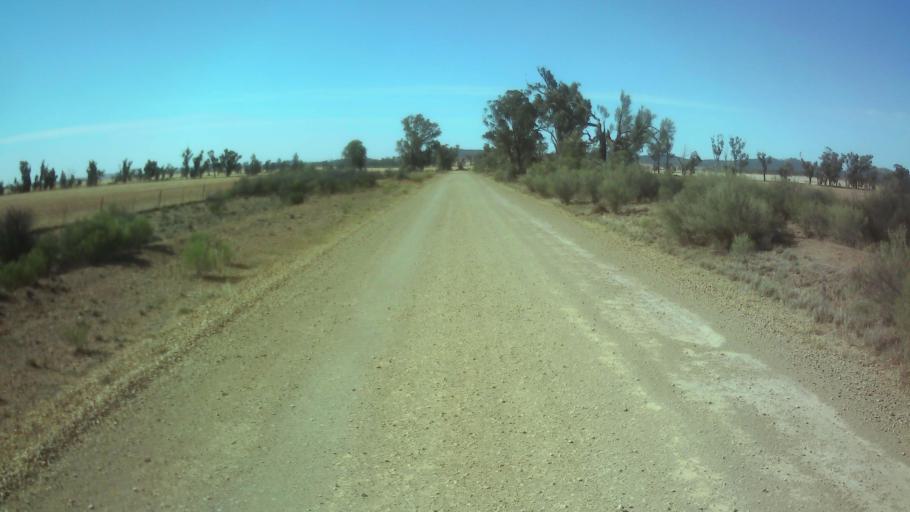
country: AU
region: New South Wales
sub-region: Forbes
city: Forbes
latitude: -33.7086
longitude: 147.7470
